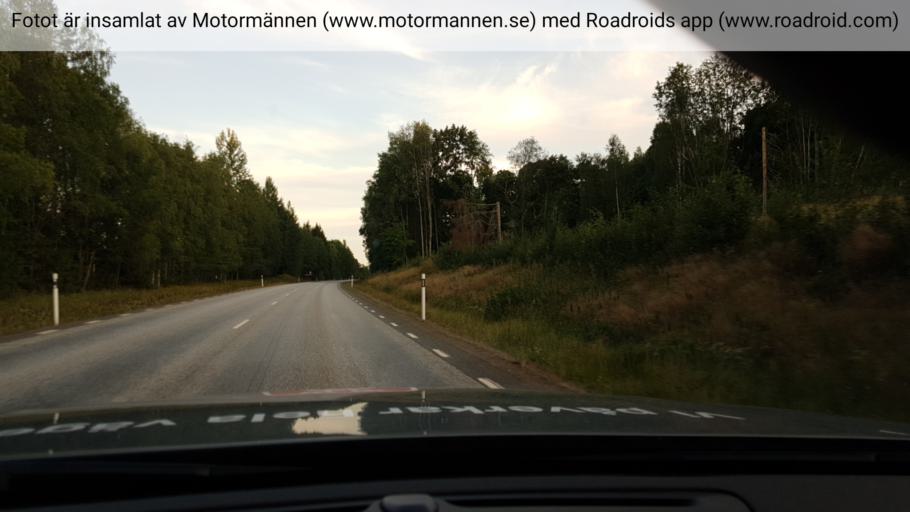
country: SE
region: Vaermland
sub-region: Storfors Kommun
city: Storfors
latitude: 59.5227
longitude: 14.3008
